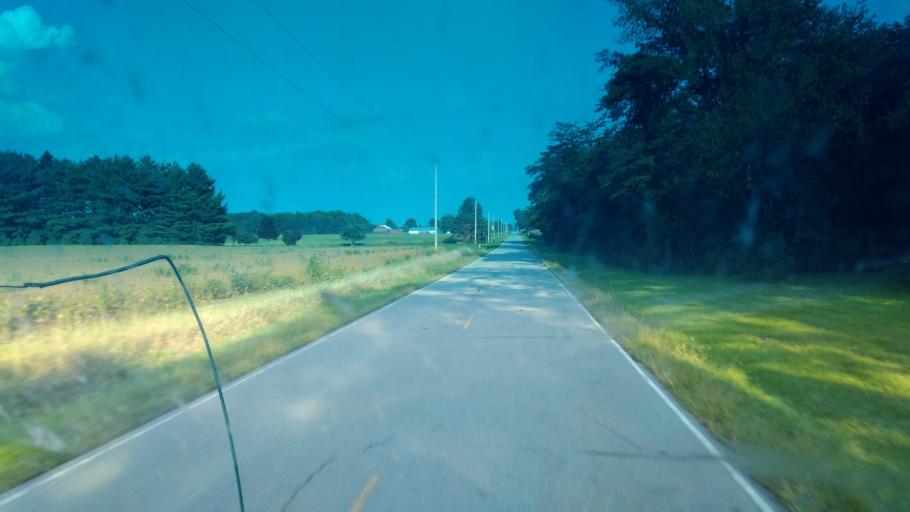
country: US
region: Ohio
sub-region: Crawford County
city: Bucyrus
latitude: 40.9650
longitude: -83.0501
